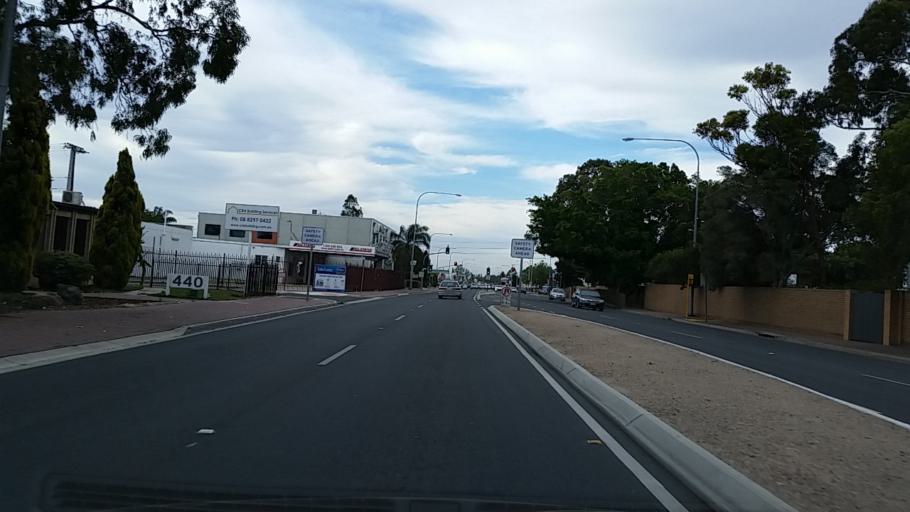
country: AU
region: South Australia
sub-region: Unley
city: Forestville
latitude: -34.9443
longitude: 138.5712
